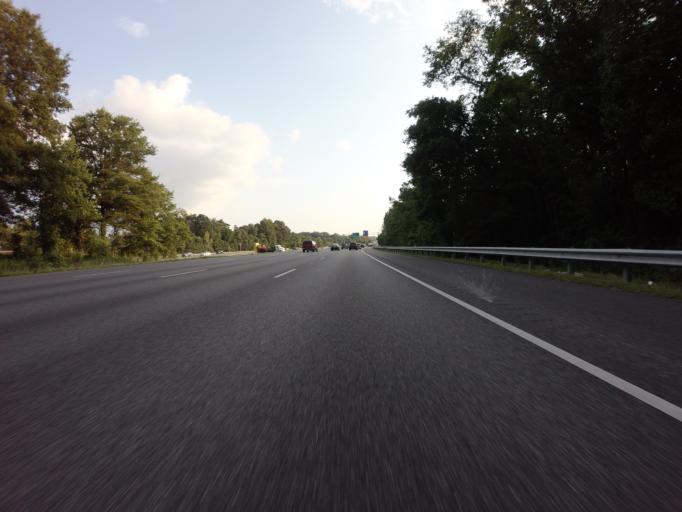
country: US
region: Maryland
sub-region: Howard County
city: North Laurel
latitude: 39.1184
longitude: -76.8701
